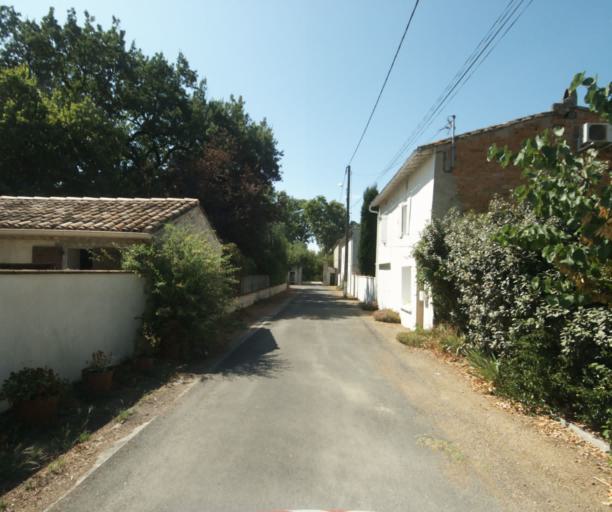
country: FR
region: Midi-Pyrenees
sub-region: Departement de la Haute-Garonne
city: Revel
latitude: 43.5014
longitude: 1.9955
